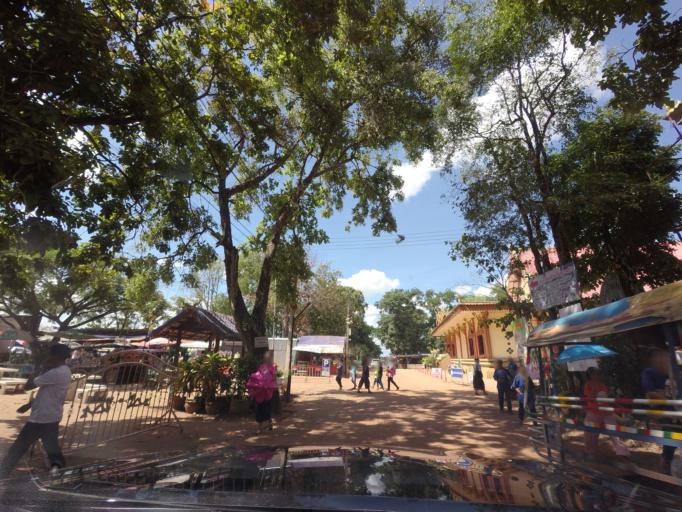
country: TH
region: Changwat Udon Thani
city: Ban Dung
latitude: 17.7428
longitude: 103.3586
